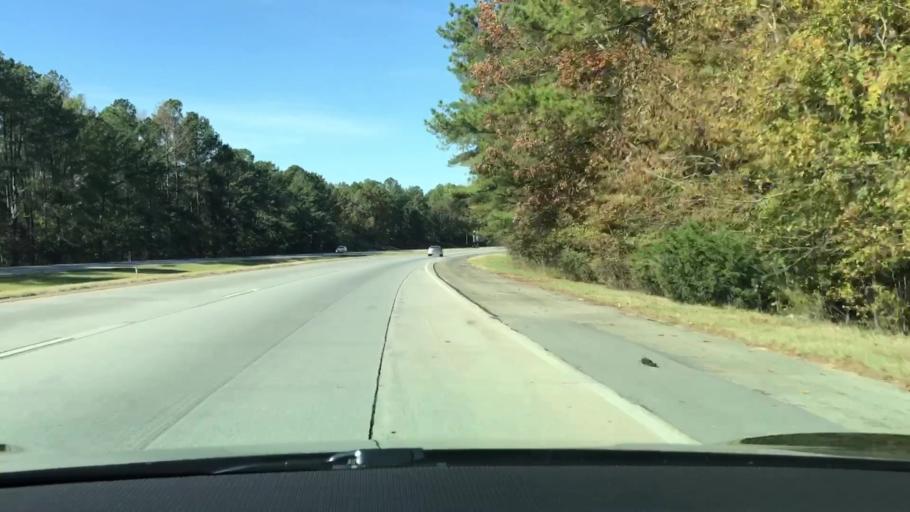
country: US
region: Georgia
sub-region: Taliaferro County
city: Crawfordville
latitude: 33.4981
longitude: -82.8132
